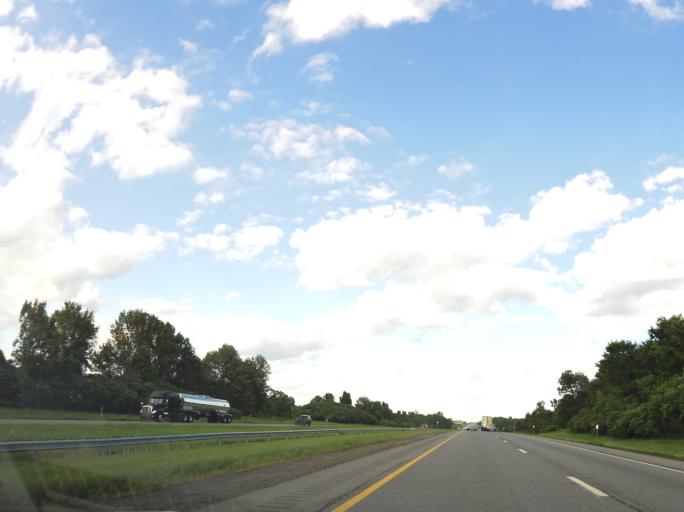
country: US
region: New York
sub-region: Genesee County
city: Oakfield
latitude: 43.0110
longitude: -78.3483
